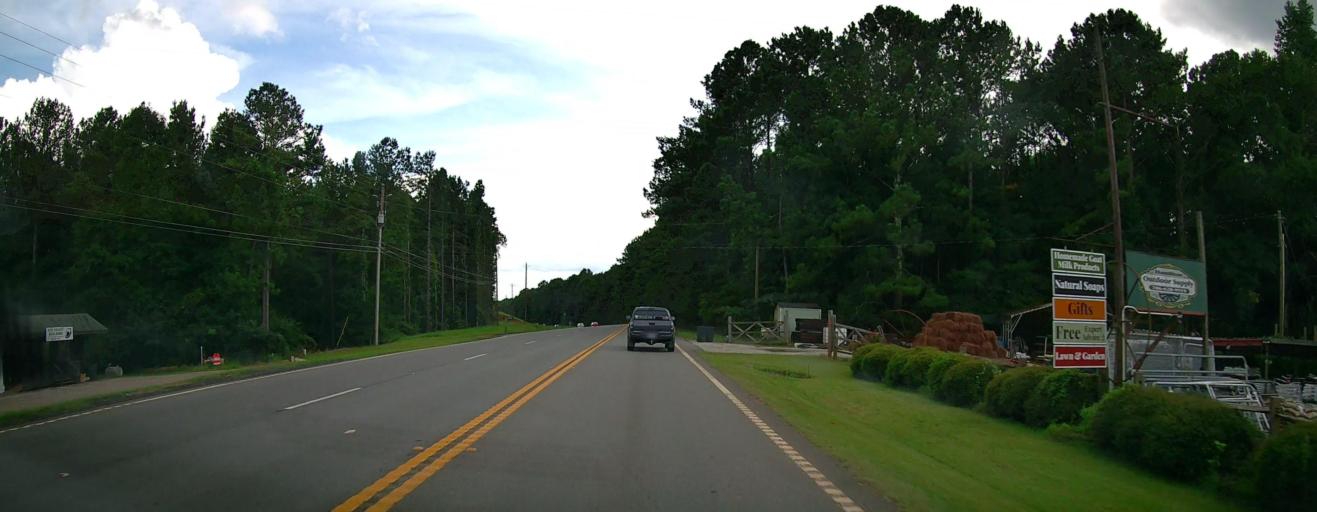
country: US
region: Georgia
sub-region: Harris County
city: Hamilton
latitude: 32.7147
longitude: -84.8725
